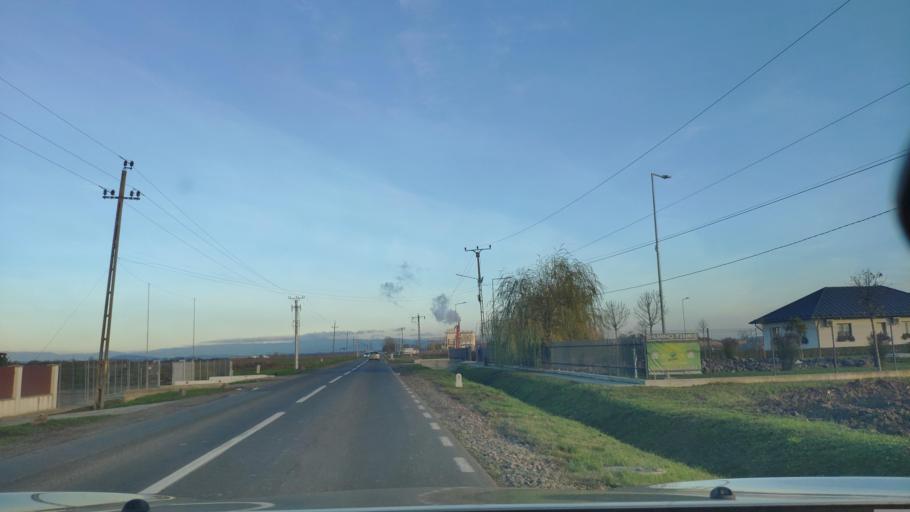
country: RO
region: Satu Mare
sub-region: Comuna Odoreu
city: Odoreu
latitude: 47.7923
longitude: 23.0154
